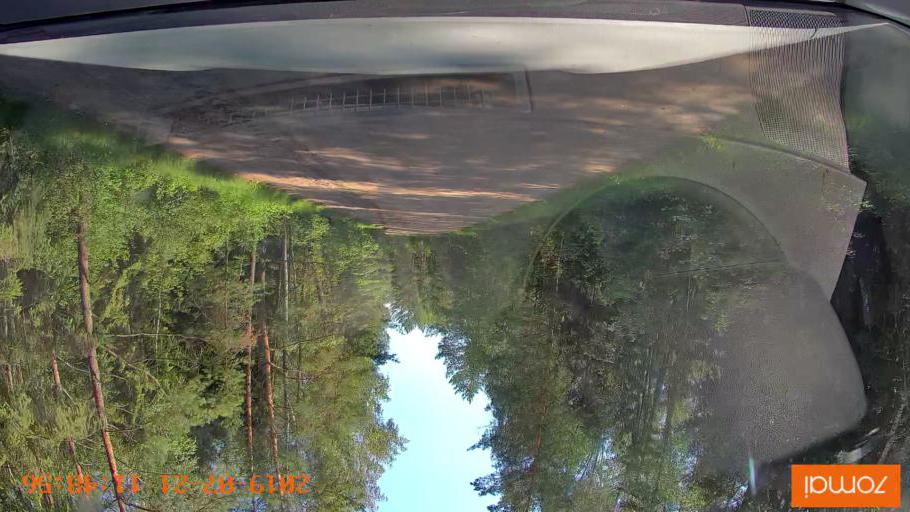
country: BY
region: Grodnenskaya
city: Lyubcha
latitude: 53.8947
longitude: 26.0443
